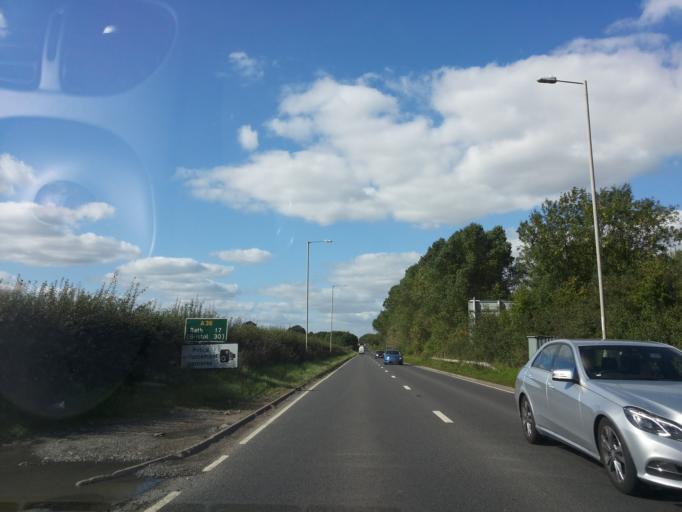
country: GB
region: England
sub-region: Wiltshire
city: Upton Scudamore
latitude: 51.2183
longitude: -2.2025
